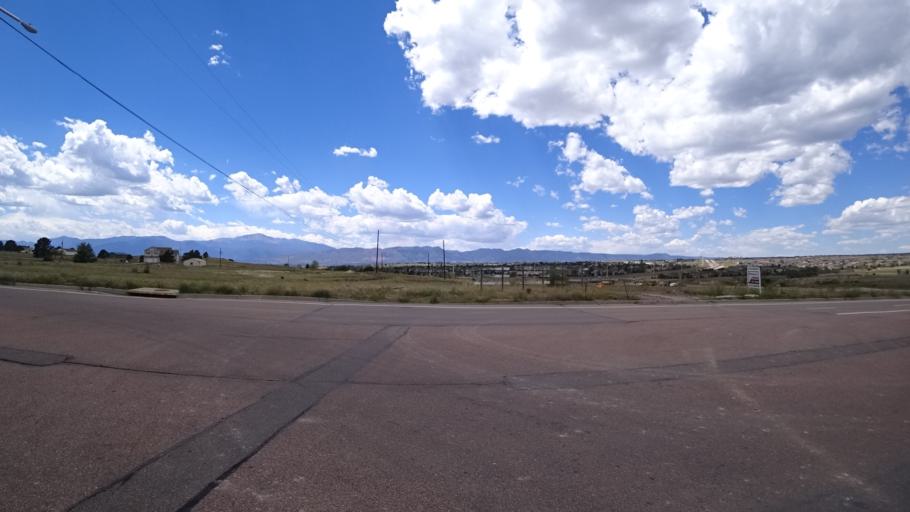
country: US
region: Colorado
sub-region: El Paso County
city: Black Forest
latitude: 38.9463
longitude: -104.7147
